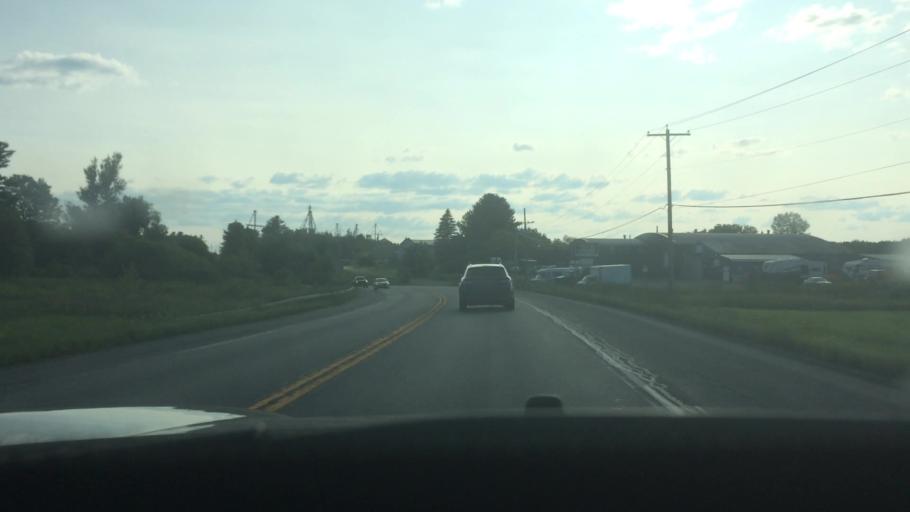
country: US
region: New York
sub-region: St. Lawrence County
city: Canton
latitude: 44.6049
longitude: -75.1327
